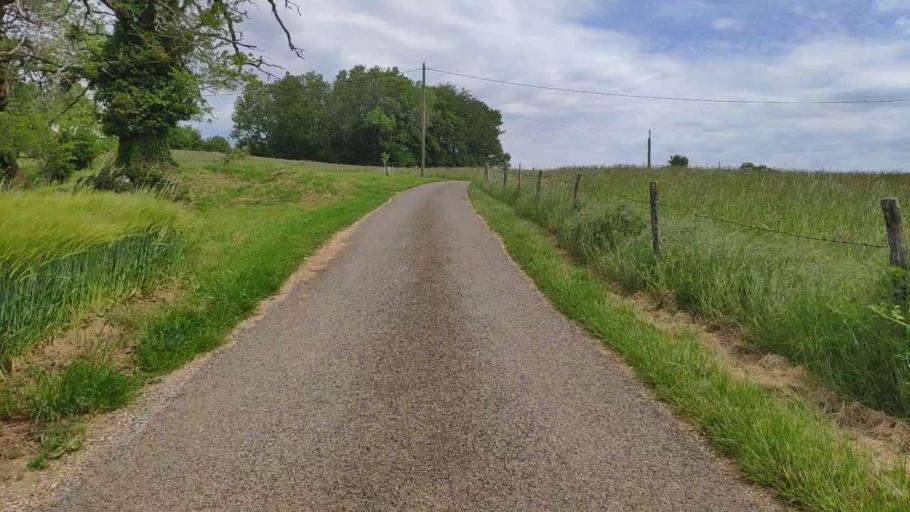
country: FR
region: Franche-Comte
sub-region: Departement du Jura
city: Poligny
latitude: 46.7900
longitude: 5.6422
